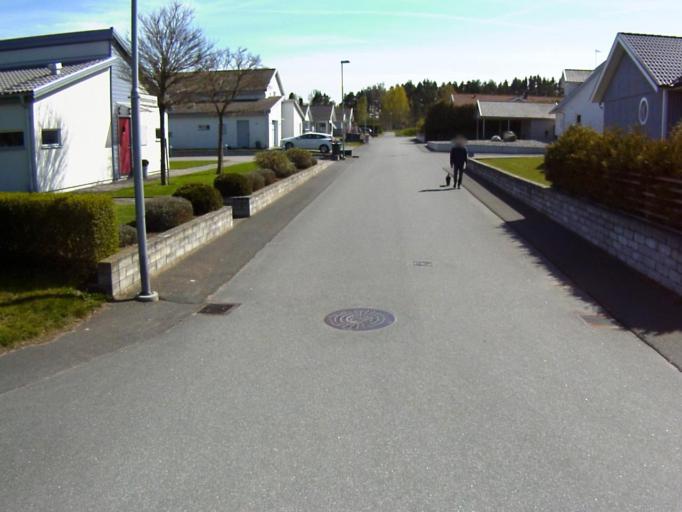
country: SE
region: Skane
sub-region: Kristianstads Kommun
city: Onnestad
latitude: 55.9979
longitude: 14.0688
